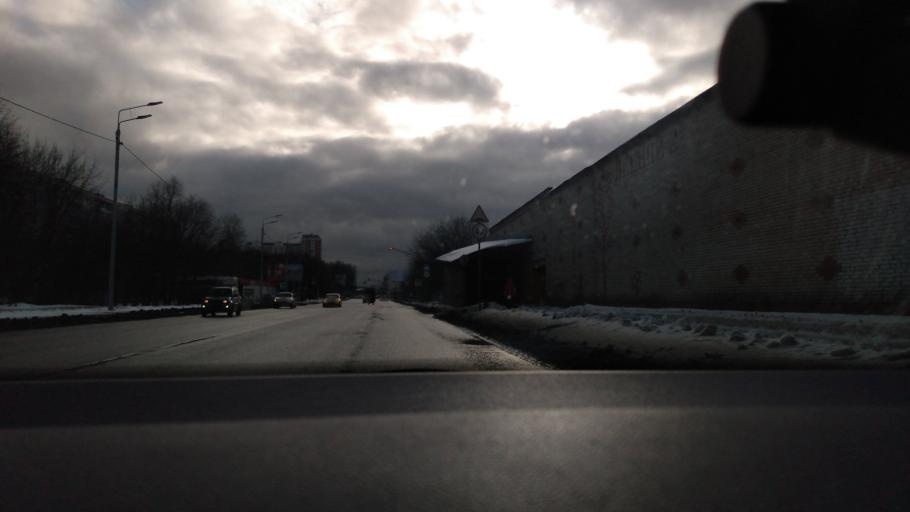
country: RU
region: Moskovskaya
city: Balashikha
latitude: 55.8228
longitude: 37.9536
